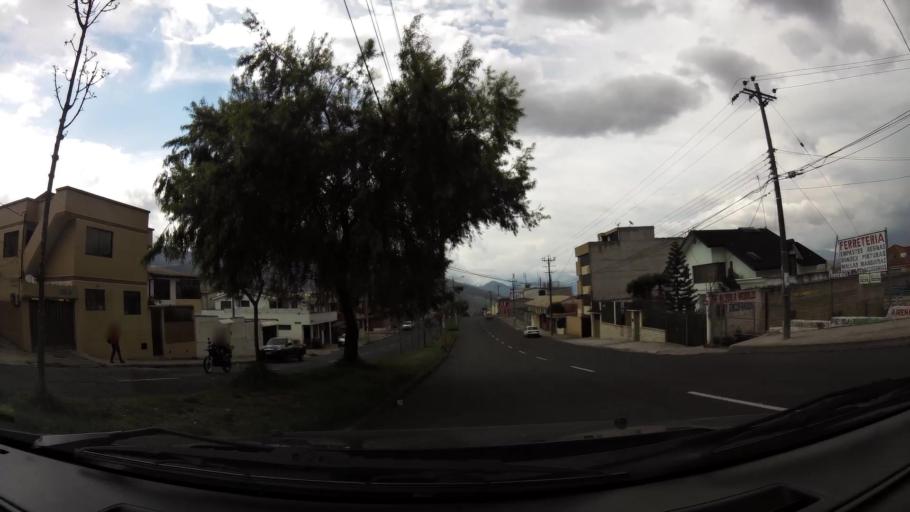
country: EC
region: Pichincha
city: Quito
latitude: -0.0891
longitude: -78.4672
